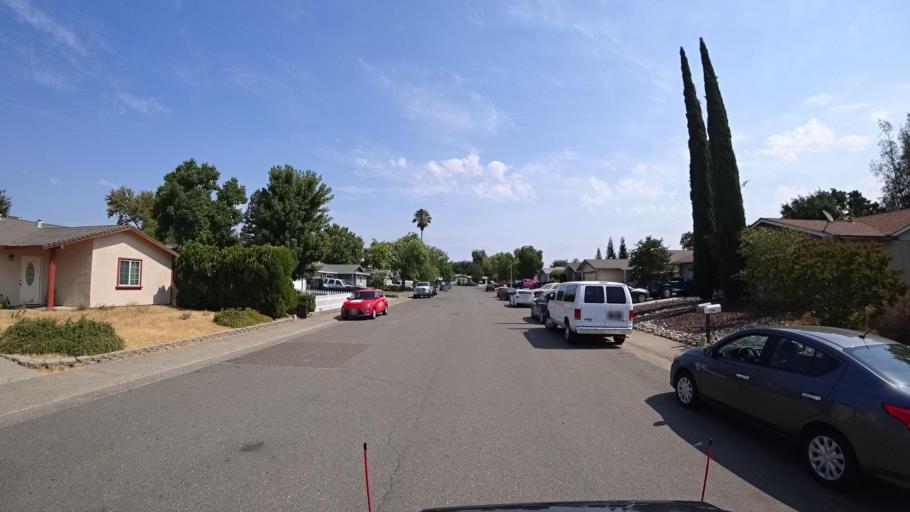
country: US
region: California
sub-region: Placer County
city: Rocklin
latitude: 38.7942
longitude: -121.2267
